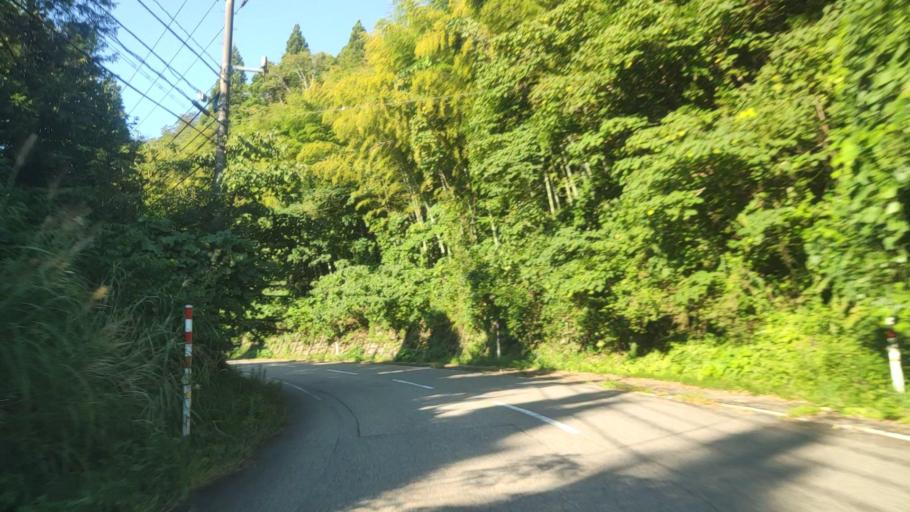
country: JP
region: Ishikawa
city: Nanao
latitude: 37.1148
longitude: 136.9658
